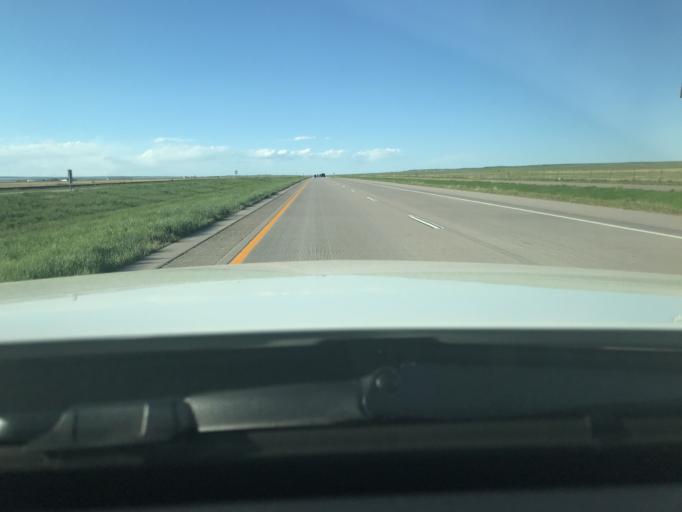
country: US
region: Colorado
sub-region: Larimer County
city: Wellington
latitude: 40.7882
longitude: -104.9833
